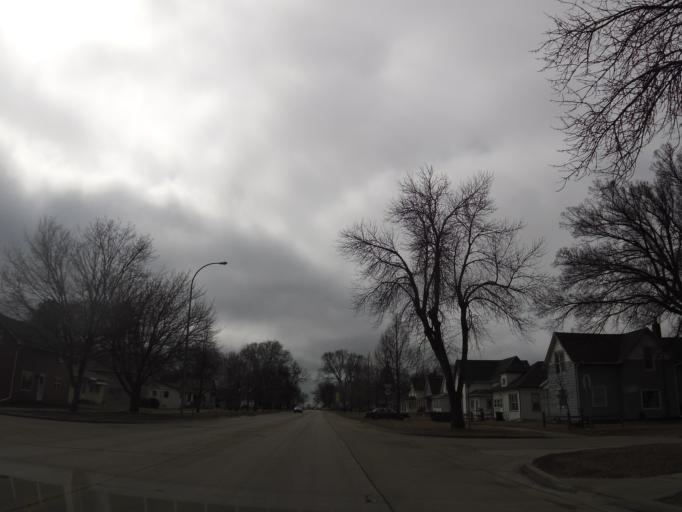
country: US
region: North Dakota
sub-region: Cass County
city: Casselton
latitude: 46.8962
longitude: -97.2118
